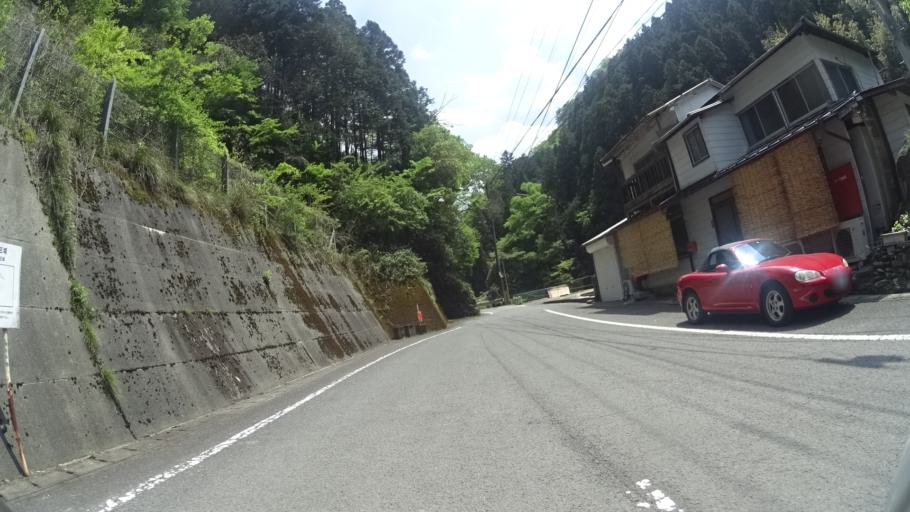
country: JP
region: Tokushima
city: Wakimachi
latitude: 33.9345
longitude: 134.0611
